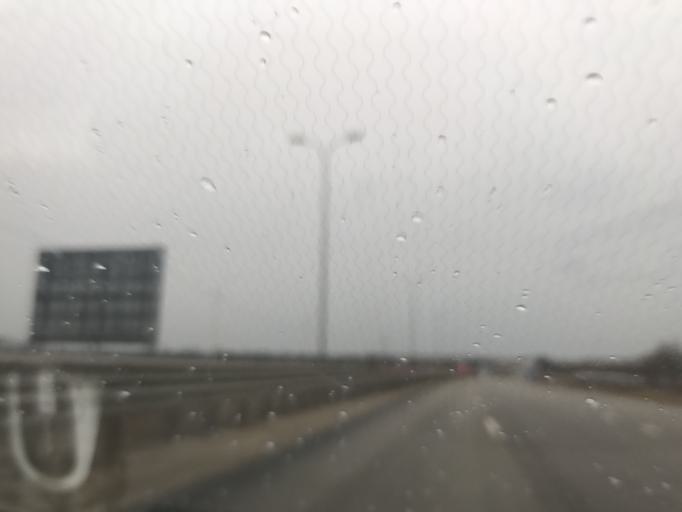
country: RU
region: Krasnodarskiy
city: Pavlovskaya
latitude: 46.1317
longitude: 39.8582
